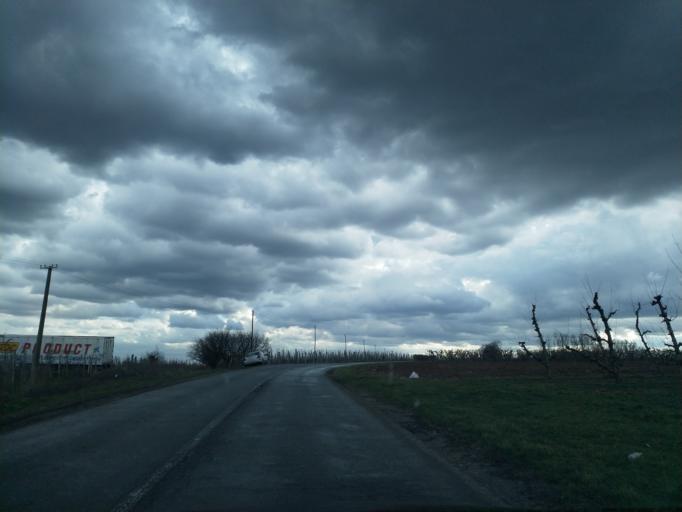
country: RS
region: Central Serbia
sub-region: Belgrade
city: Grocka
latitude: 44.6396
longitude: 20.7510
